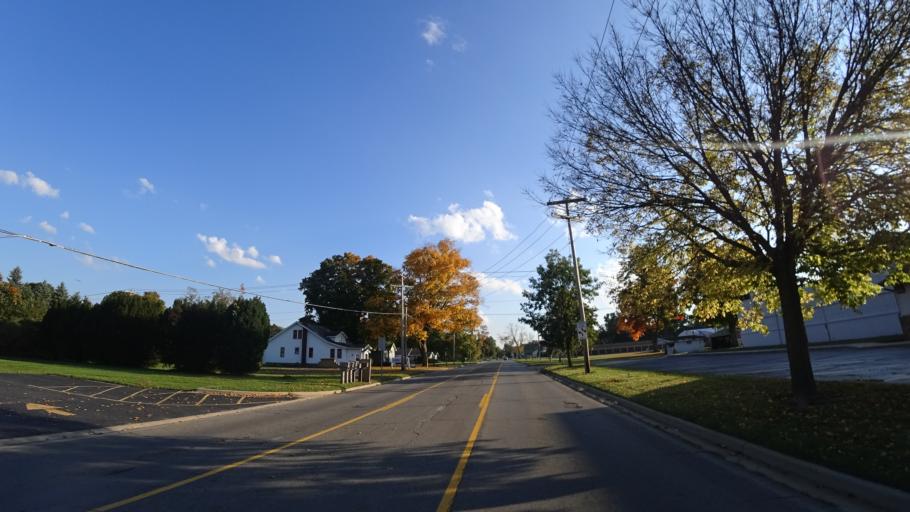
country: US
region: Michigan
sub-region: Saint Joseph County
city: Three Rivers
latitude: 41.9624
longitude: -85.6348
